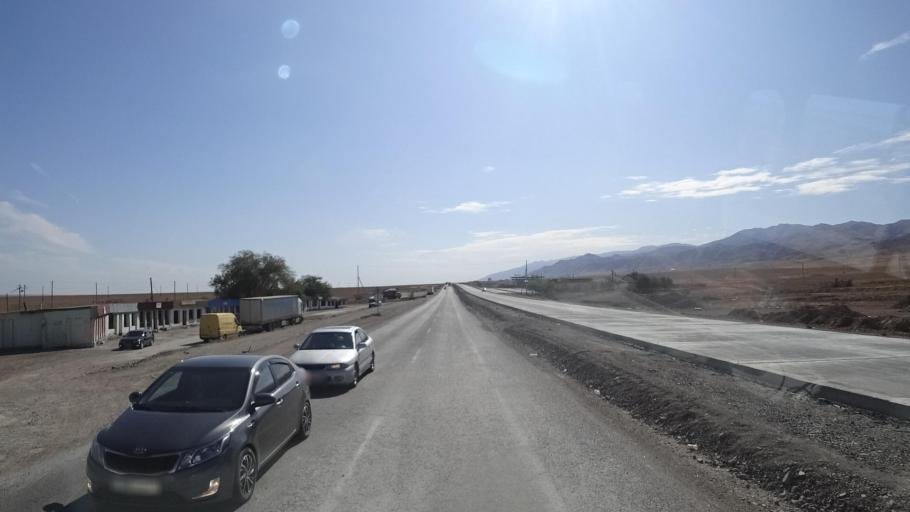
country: KG
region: Chuy
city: Ivanovka
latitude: 43.4013
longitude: 75.1118
